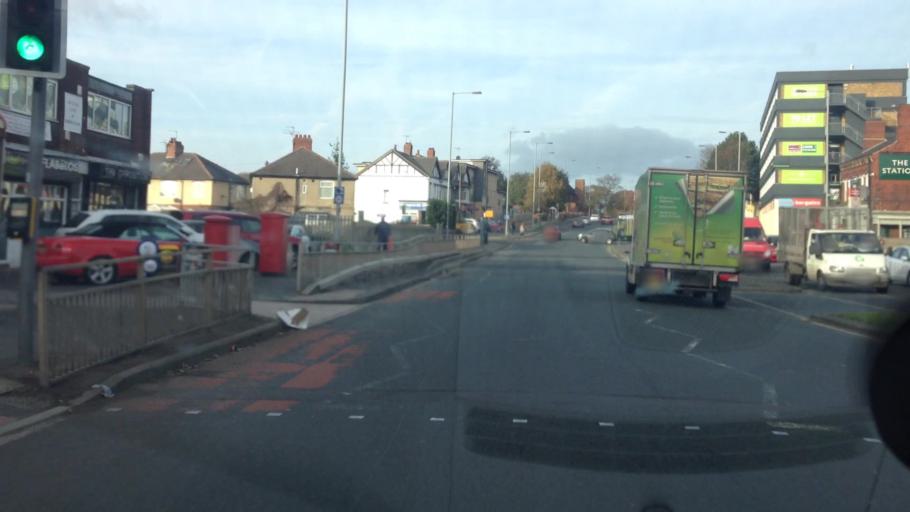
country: GB
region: England
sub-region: City and Borough of Leeds
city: Scholes
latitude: 53.8043
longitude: -1.4521
